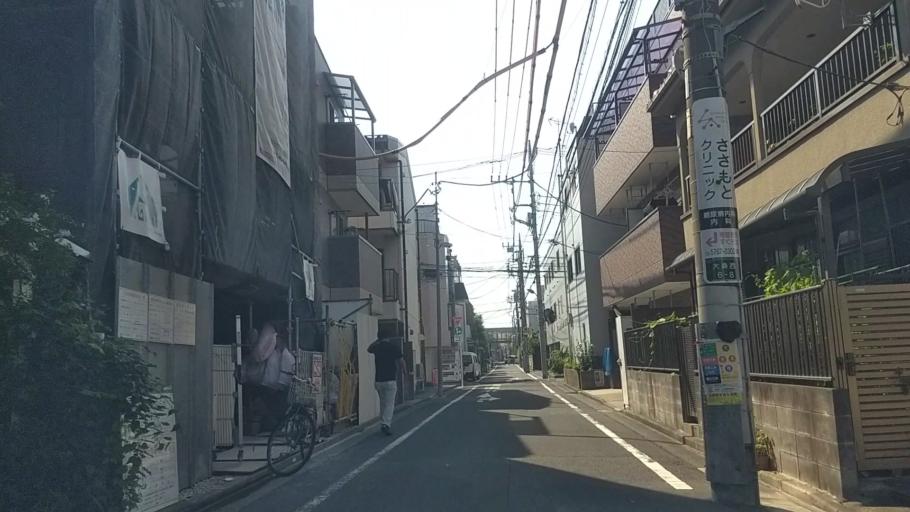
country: JP
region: Kanagawa
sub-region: Kawasaki-shi
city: Kawasaki
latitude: 35.5687
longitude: 139.7264
